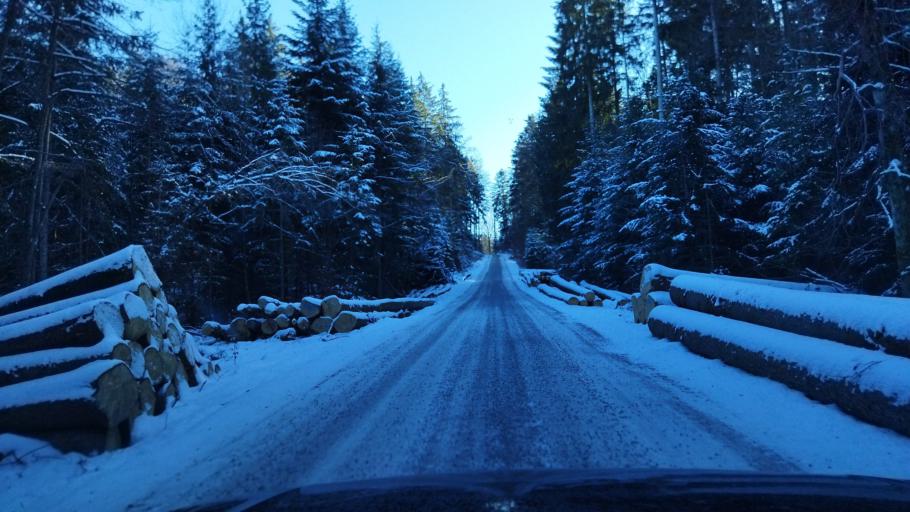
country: DE
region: Baden-Wuerttemberg
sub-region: Regierungsbezirk Stuttgart
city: Gerabronn
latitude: 48.9650
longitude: 9.9175
